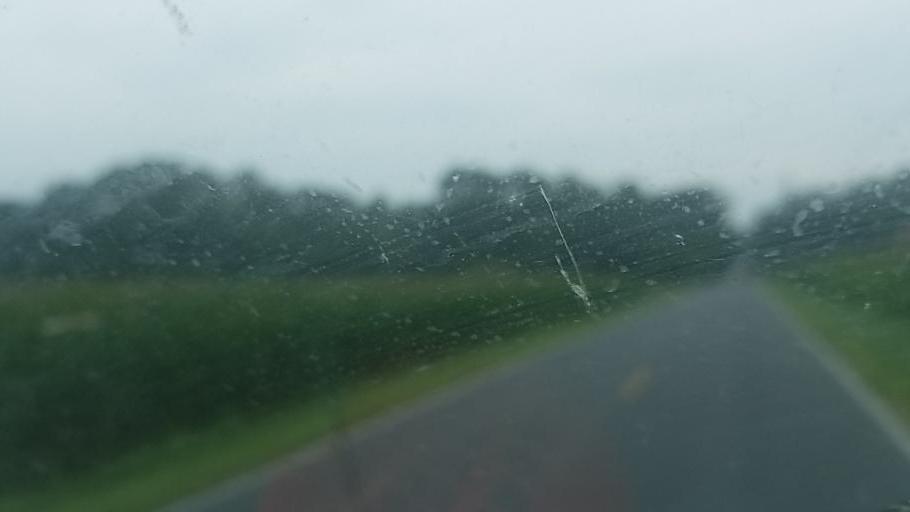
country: US
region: Maryland
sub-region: Wicomico County
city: Salisbury
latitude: 38.3932
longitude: -75.5311
